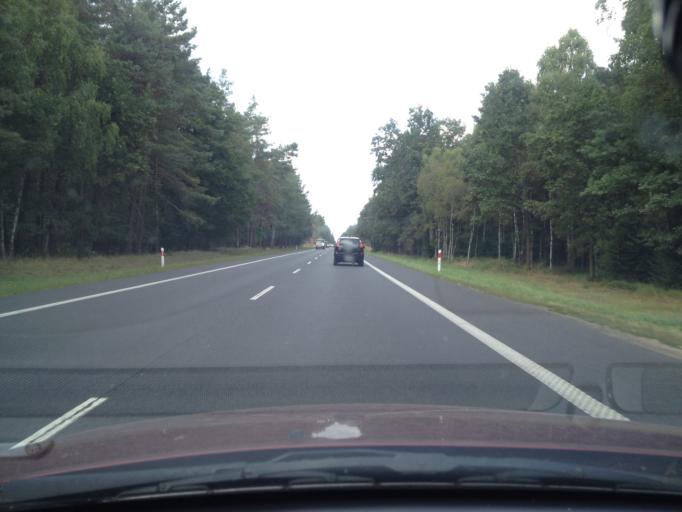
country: PL
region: West Pomeranian Voivodeship
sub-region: Powiat goleniowski
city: Goleniow
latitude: 53.6399
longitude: 14.8173
